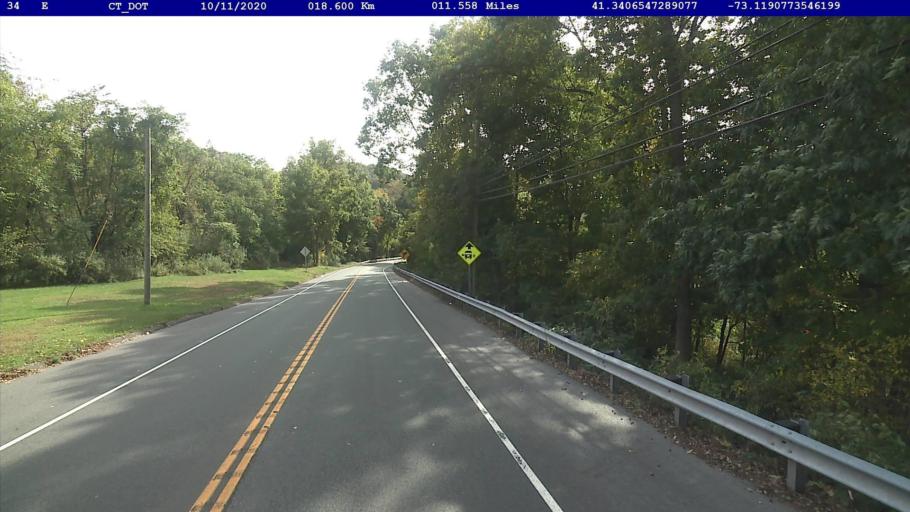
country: US
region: Connecticut
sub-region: Fairfield County
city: Shelton
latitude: 41.3406
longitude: -73.1192
